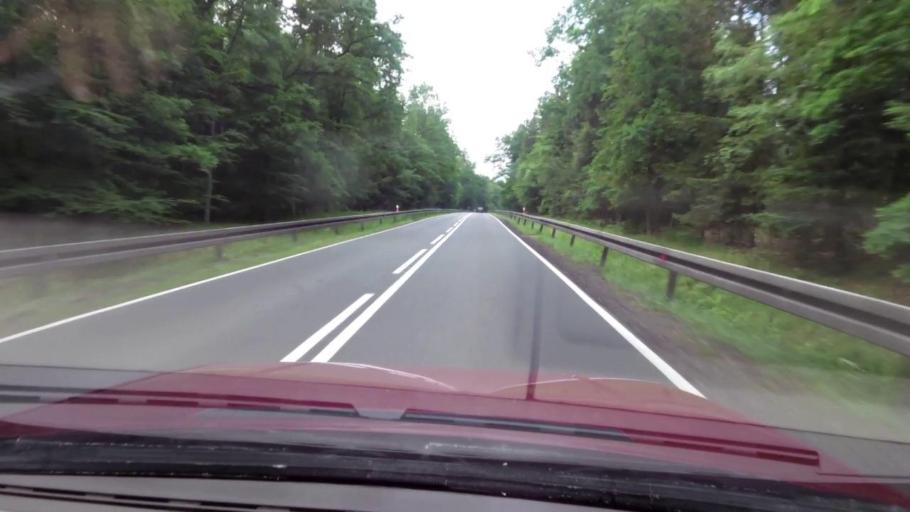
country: PL
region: Pomeranian Voivodeship
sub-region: Powiat bytowski
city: Trzebielino
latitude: 54.2285
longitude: 17.0867
